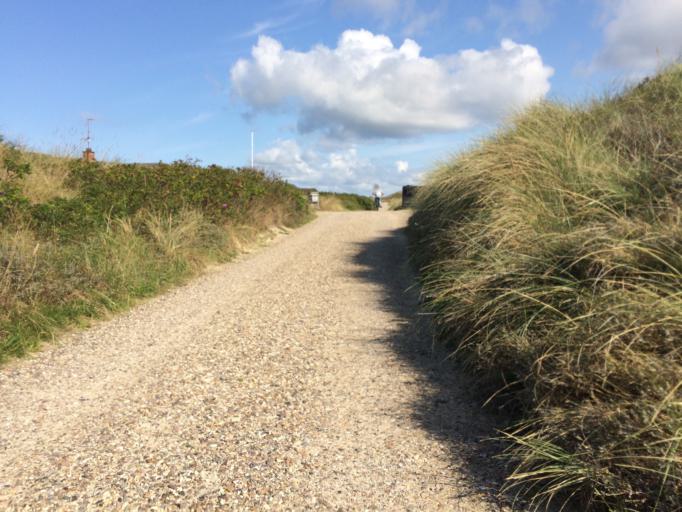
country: DK
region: Central Jutland
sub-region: Ringkobing-Skjern Kommune
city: Hvide Sande
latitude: 55.9259
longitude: 8.1509
